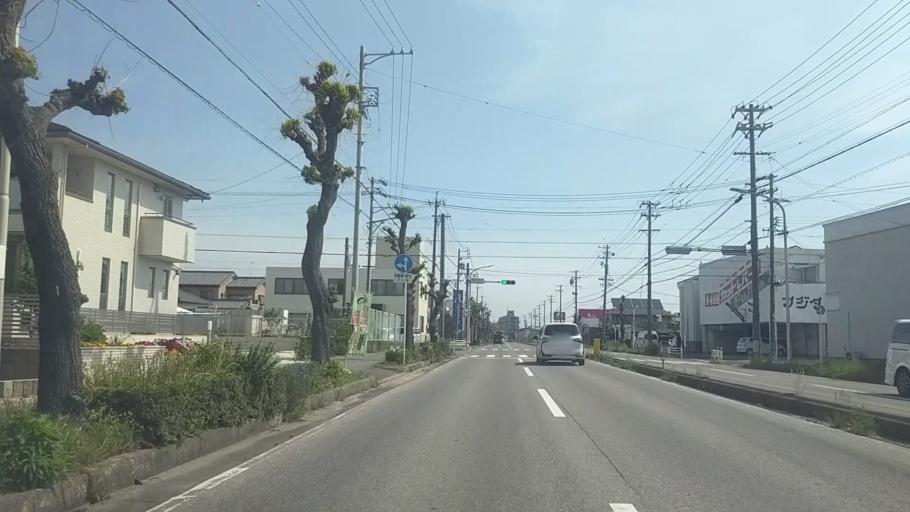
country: JP
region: Aichi
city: Anjo
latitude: 34.9507
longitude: 137.0956
